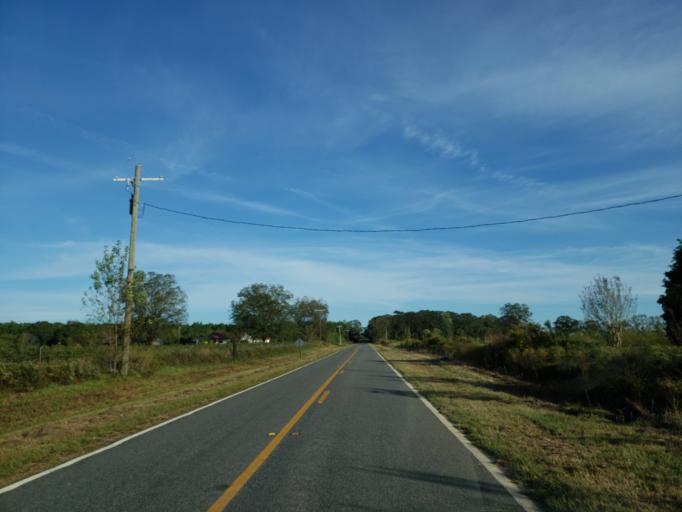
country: US
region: Georgia
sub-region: Dooly County
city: Vienna
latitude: 32.0322
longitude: -83.7501
